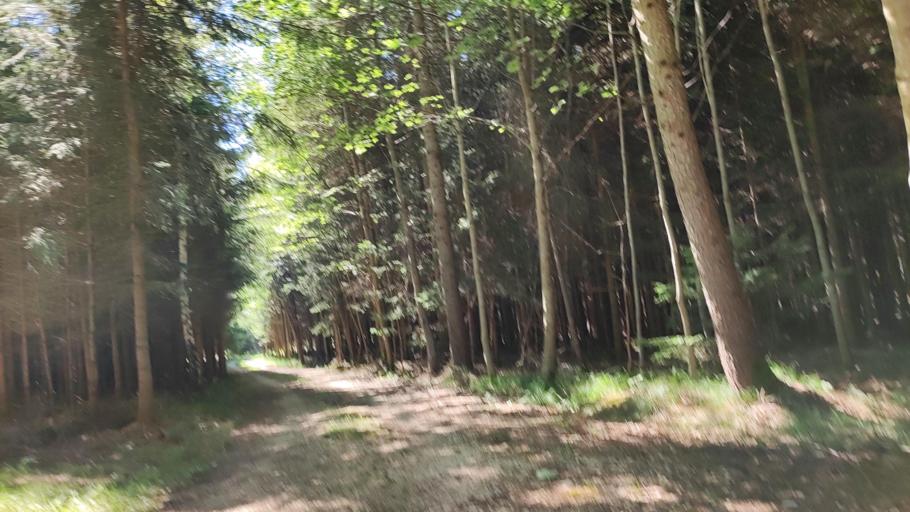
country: DE
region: Bavaria
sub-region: Swabia
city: Landensberg
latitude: 48.4623
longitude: 10.5282
